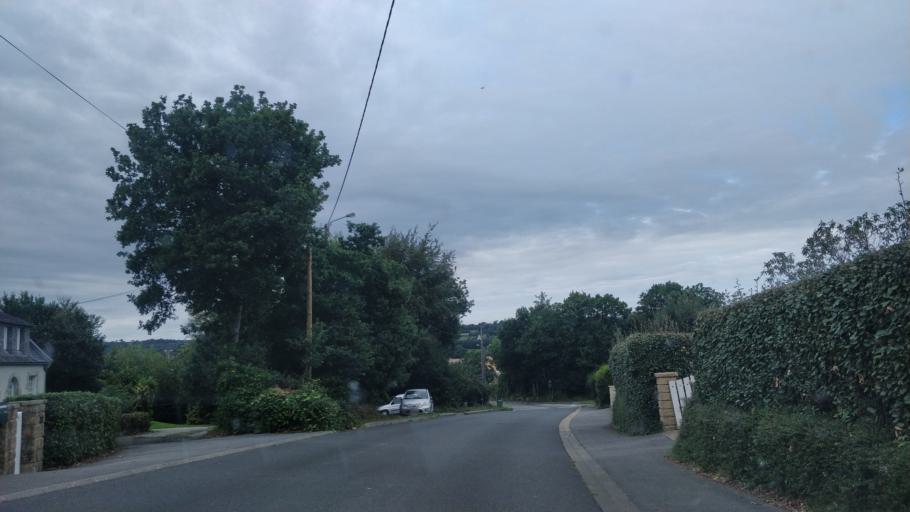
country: FR
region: Brittany
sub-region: Departement du Finistere
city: Loperhet
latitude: 48.3782
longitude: -4.3058
